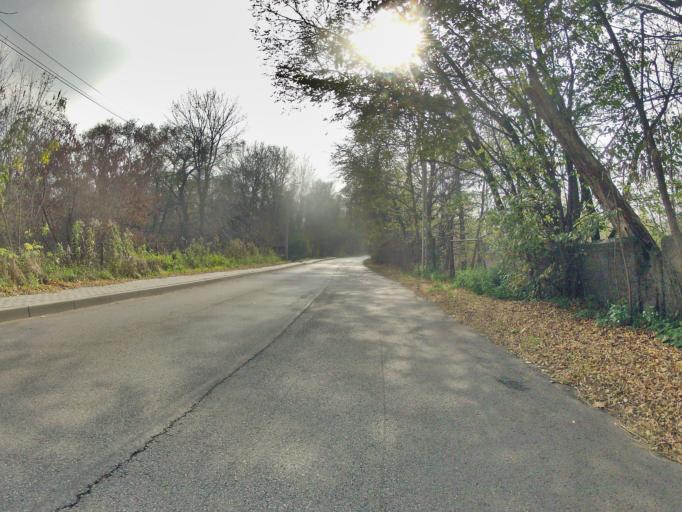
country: PL
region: Lesser Poland Voivodeship
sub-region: Powiat wielicki
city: Wegrzce Wielkie
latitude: 50.0672
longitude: 20.1095
